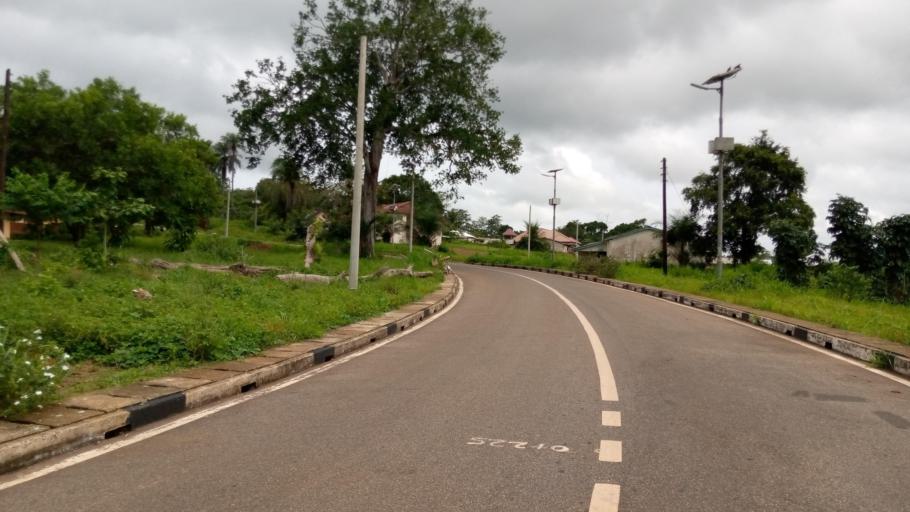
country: SL
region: Southern Province
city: Moyamba
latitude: 8.1619
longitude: -12.4395
